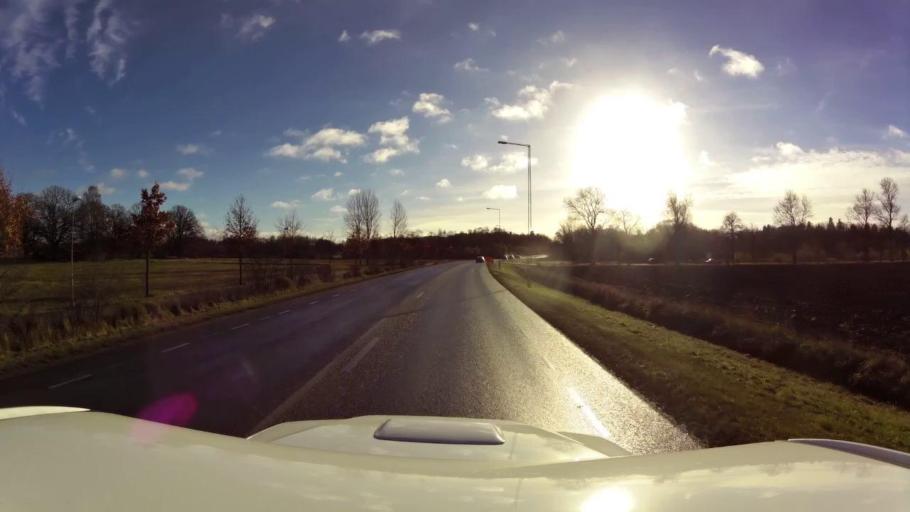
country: SE
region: OEstergoetland
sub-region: Linkopings Kommun
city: Linkoping
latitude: 58.3881
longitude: 15.6278
